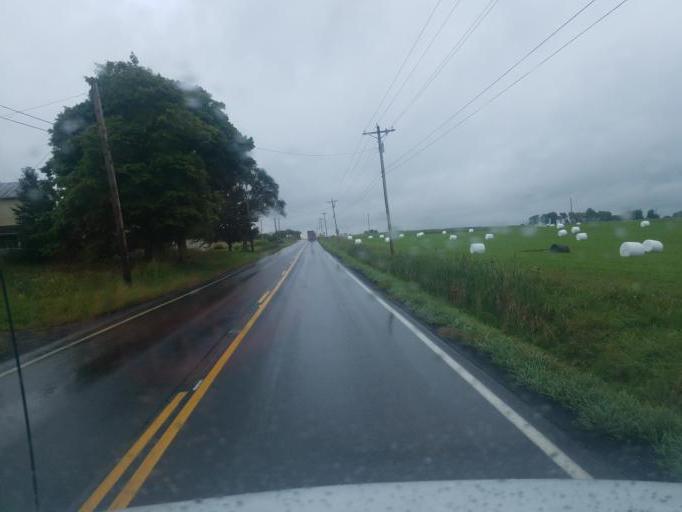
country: US
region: Ohio
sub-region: Wayne County
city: West Salem
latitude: 40.9359
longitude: -82.0819
